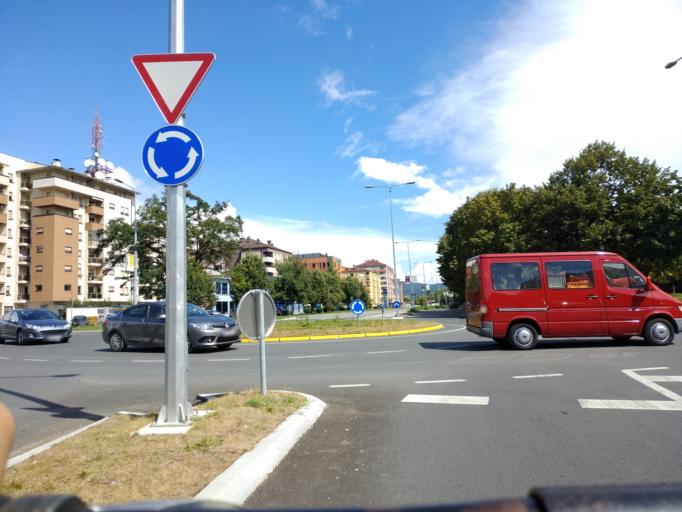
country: BA
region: Republika Srpska
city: Mejdan - Obilicevo
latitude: 44.7621
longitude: 17.2010
